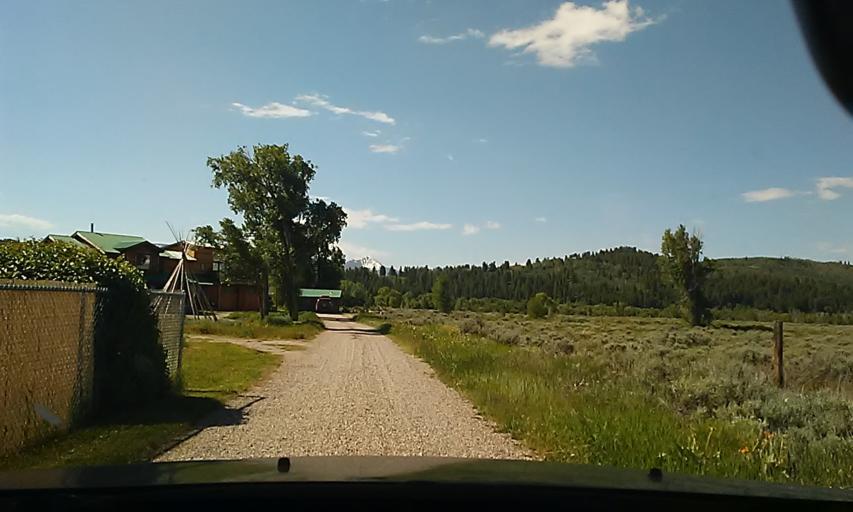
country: US
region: Wyoming
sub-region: Teton County
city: Jackson
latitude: 43.6248
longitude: -110.6288
